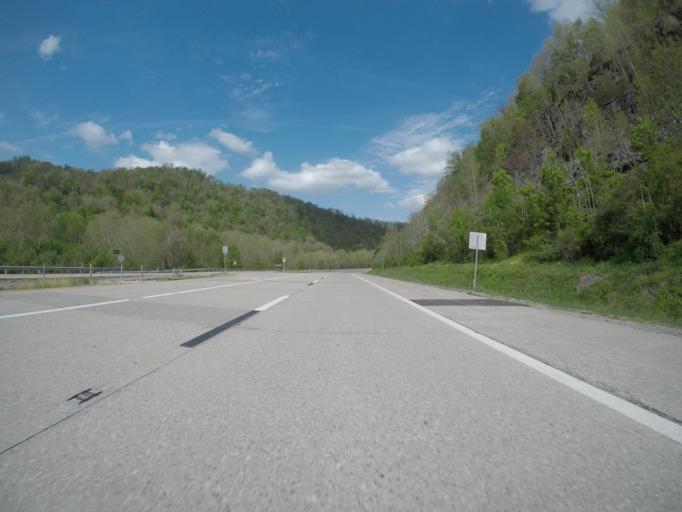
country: US
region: West Virginia
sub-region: Boone County
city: Madison
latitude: 38.1394
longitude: -81.8404
